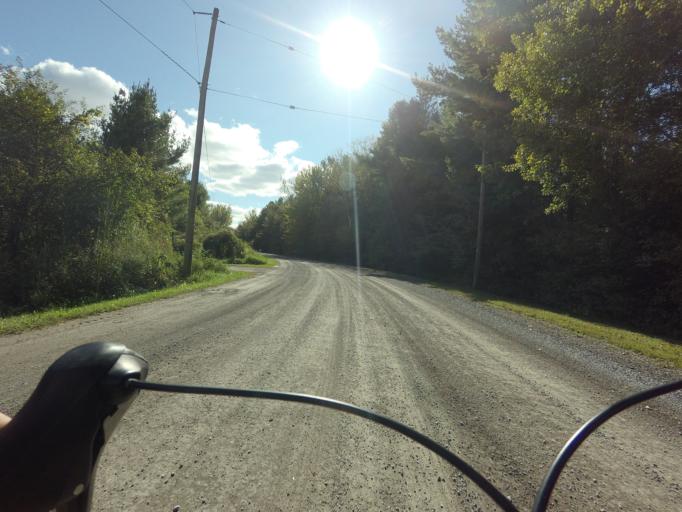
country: CA
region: Ontario
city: Bells Corners
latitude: 45.1036
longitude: -75.6220
